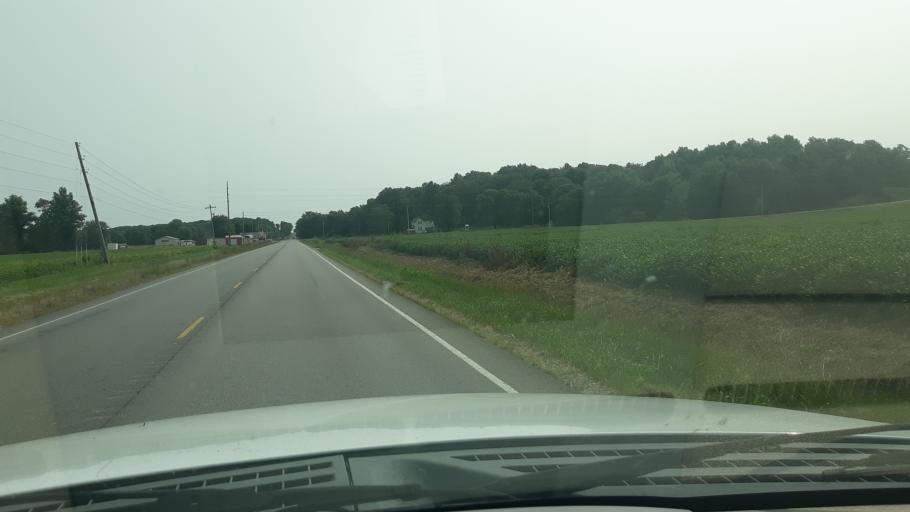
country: US
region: Indiana
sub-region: Gibson County
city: Owensville
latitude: 38.3559
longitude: -87.6765
